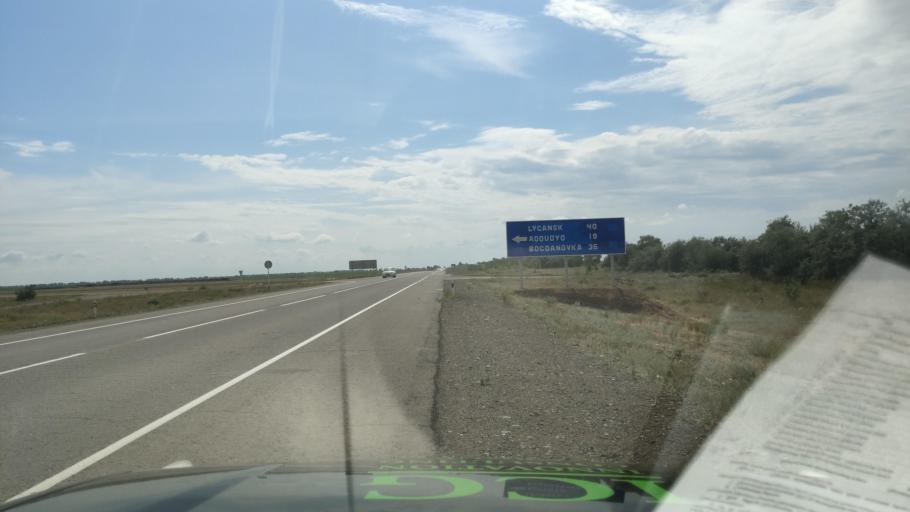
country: KZ
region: Pavlodar
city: Leninskiy
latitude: 52.6380
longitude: 76.7515
